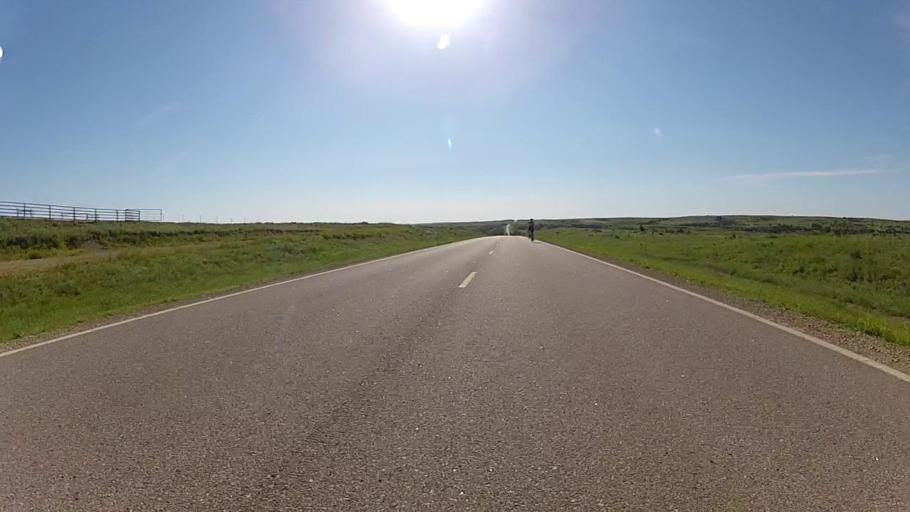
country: US
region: Kansas
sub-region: Barber County
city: Medicine Lodge
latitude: 37.2816
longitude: -98.8841
